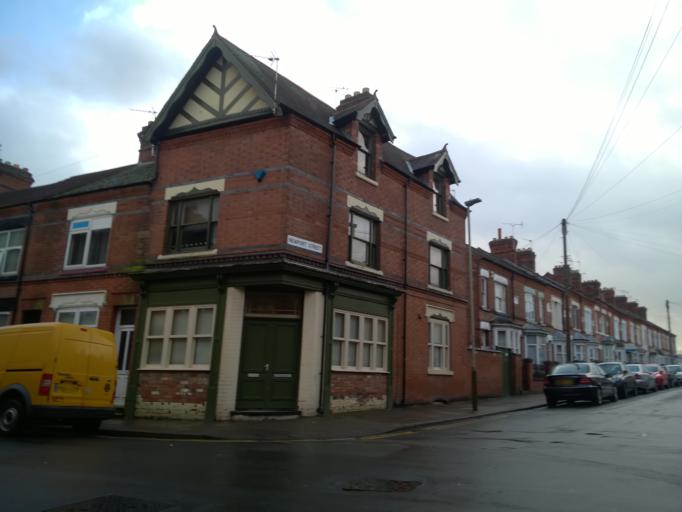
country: GB
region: England
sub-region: City of Leicester
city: Leicester
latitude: 52.6411
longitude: -1.1524
